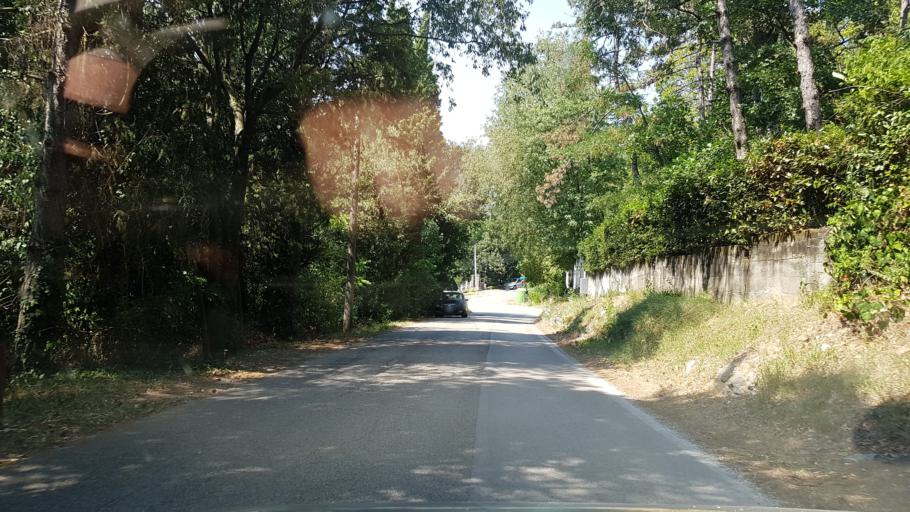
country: IT
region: Friuli Venezia Giulia
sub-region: Provincia di Gorizia
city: Sagrado
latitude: 45.8752
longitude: 13.4908
